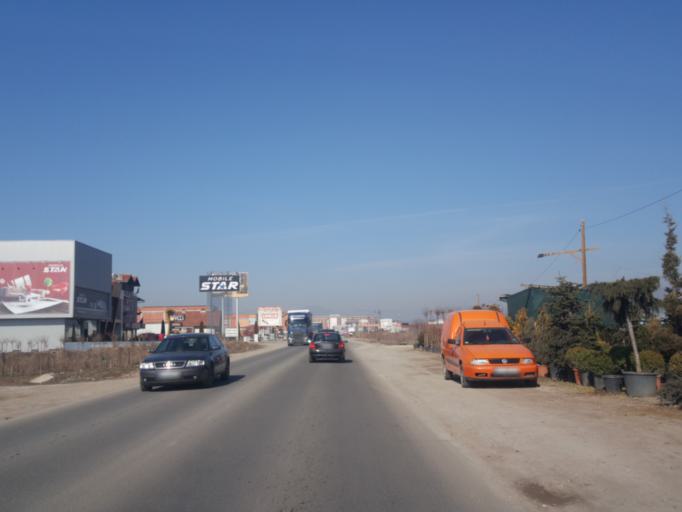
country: XK
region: Mitrovica
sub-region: Vushtrri
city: Vushtrri
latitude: 42.8106
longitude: 20.9867
